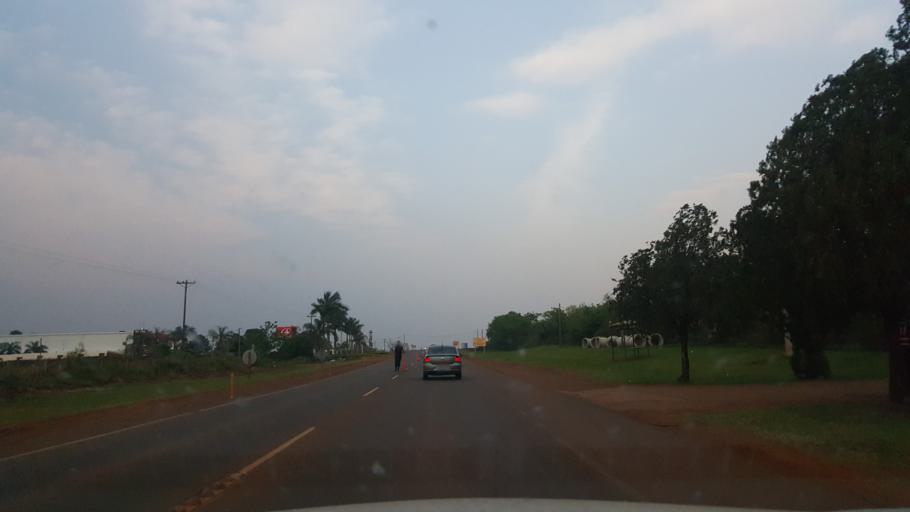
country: AR
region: Misiones
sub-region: Departamento de Capital
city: Posadas
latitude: -27.4094
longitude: -55.9772
